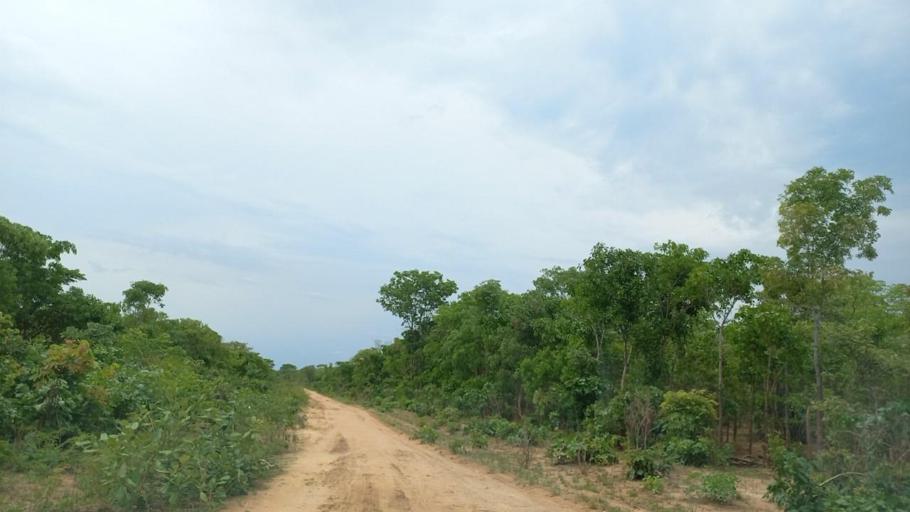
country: ZM
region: North-Western
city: Mufumbwe
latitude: -13.6521
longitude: 24.9786
